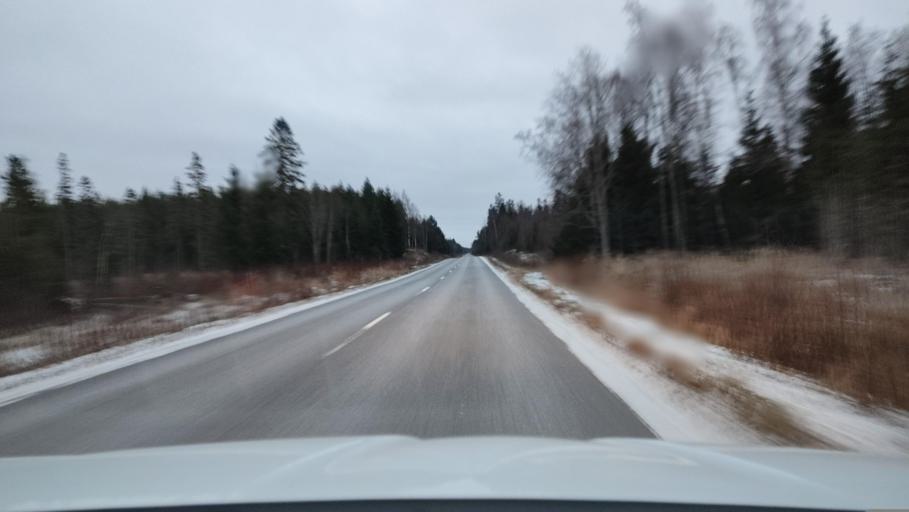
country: FI
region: Ostrobothnia
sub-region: Vaasa
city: Replot
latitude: 63.2582
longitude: 21.3652
